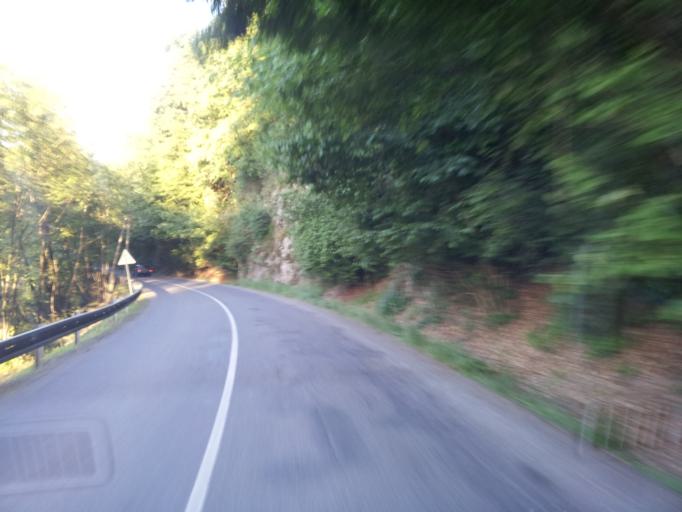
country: SK
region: Banskobystricky
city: Svaety Anton
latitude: 48.3311
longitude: 18.9677
